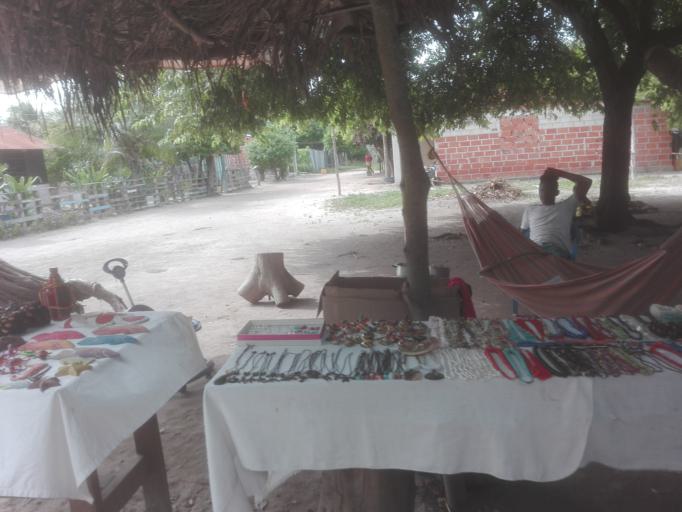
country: CO
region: Bolivar
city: Turbana
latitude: 10.1770
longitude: -75.7412
